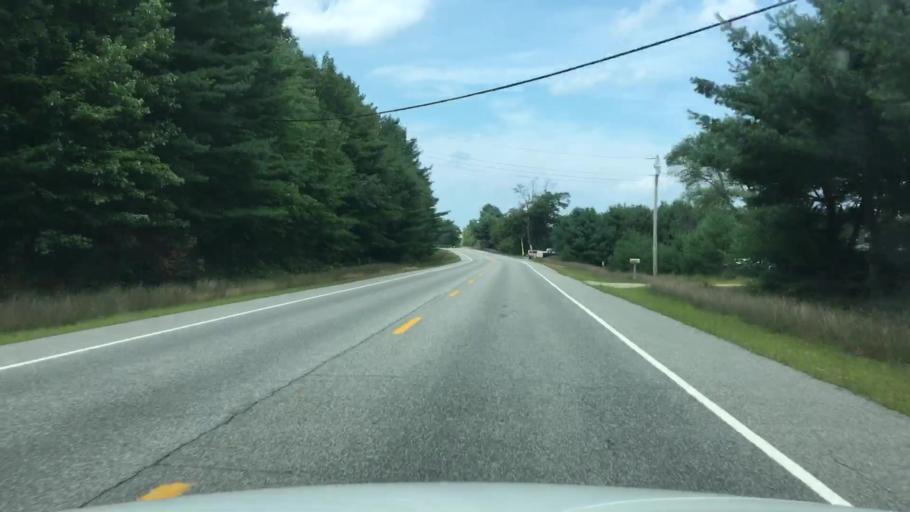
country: US
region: Maine
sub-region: Oxford County
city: Canton
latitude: 44.4309
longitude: -70.3018
